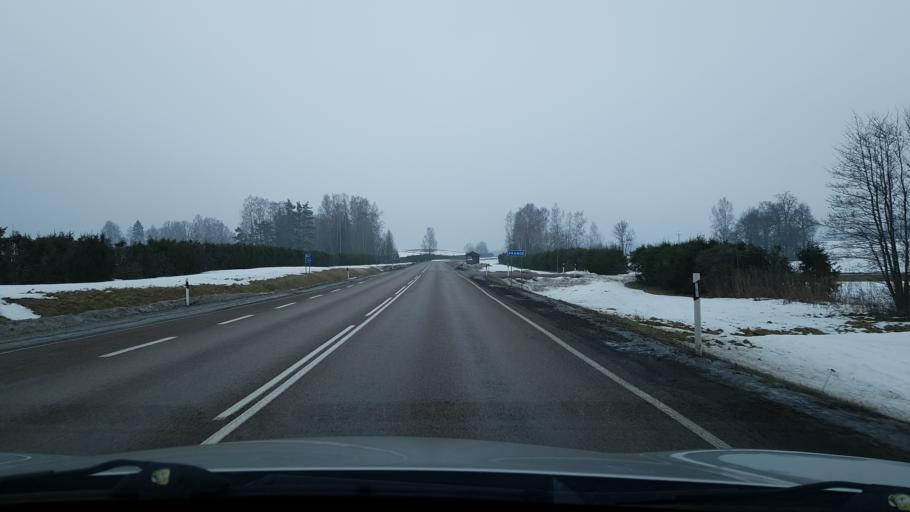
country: EE
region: Valgamaa
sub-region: Torva linn
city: Torva
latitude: 58.0391
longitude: 26.1851
